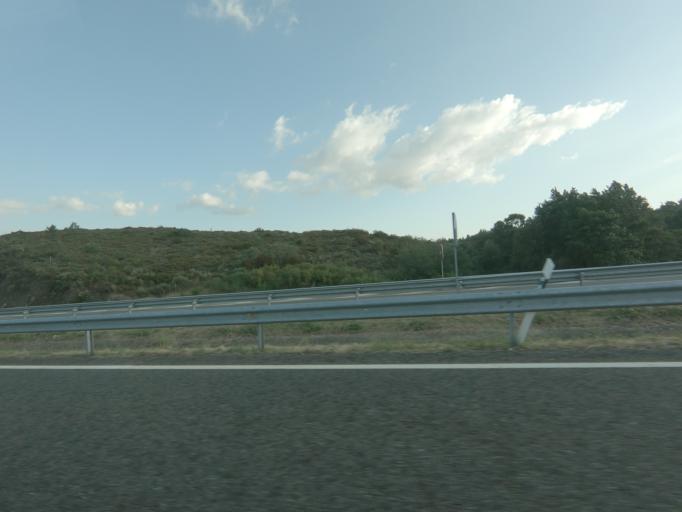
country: ES
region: Galicia
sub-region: Provincia de Ourense
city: Cualedro
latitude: 41.9809
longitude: -7.5405
